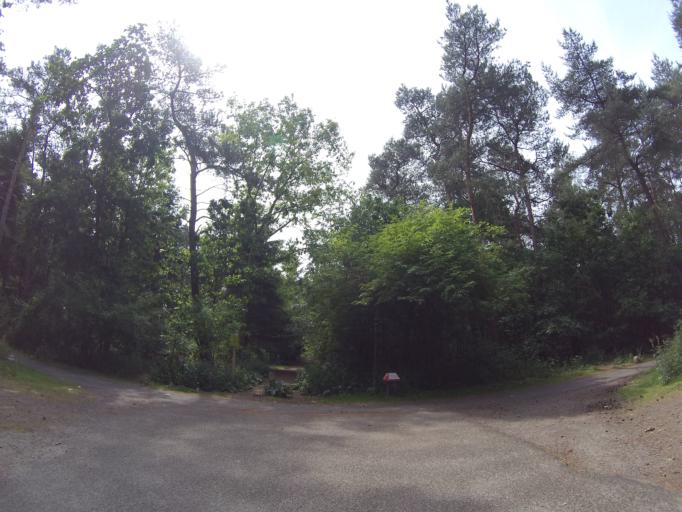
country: NL
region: Utrecht
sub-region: Gemeente Zeist
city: Zeist
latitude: 52.1111
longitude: 5.2829
